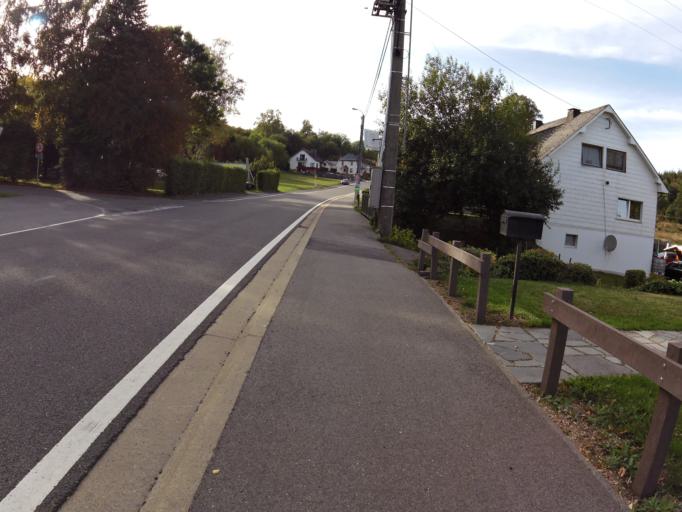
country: BE
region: Wallonia
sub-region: Province de Liege
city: Saint-Vith
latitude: 50.2641
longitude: 6.1433
